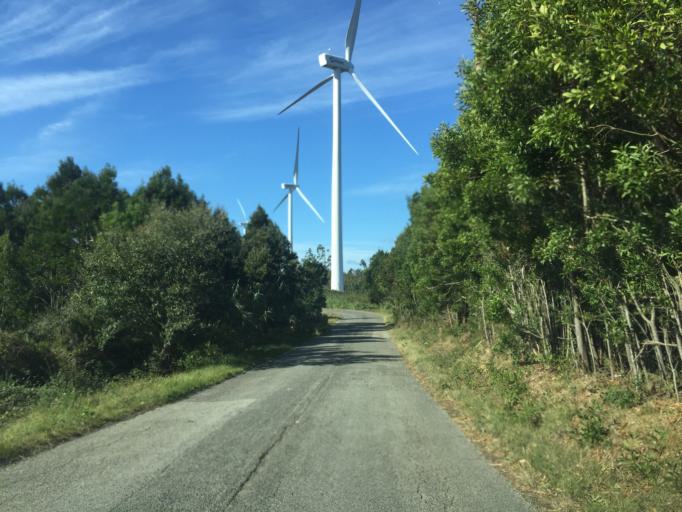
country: PT
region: Coimbra
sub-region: Figueira da Foz
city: Tavarede
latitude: 40.1952
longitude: -8.8516
